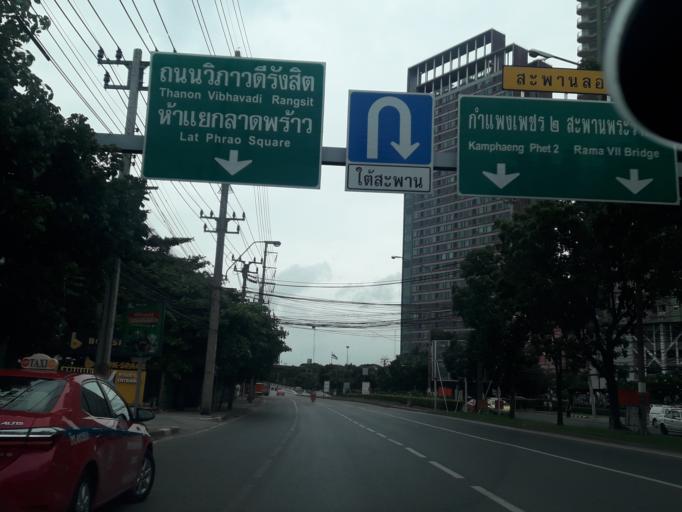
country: TH
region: Bangkok
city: Chatuchak
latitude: 13.8298
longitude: 100.5622
